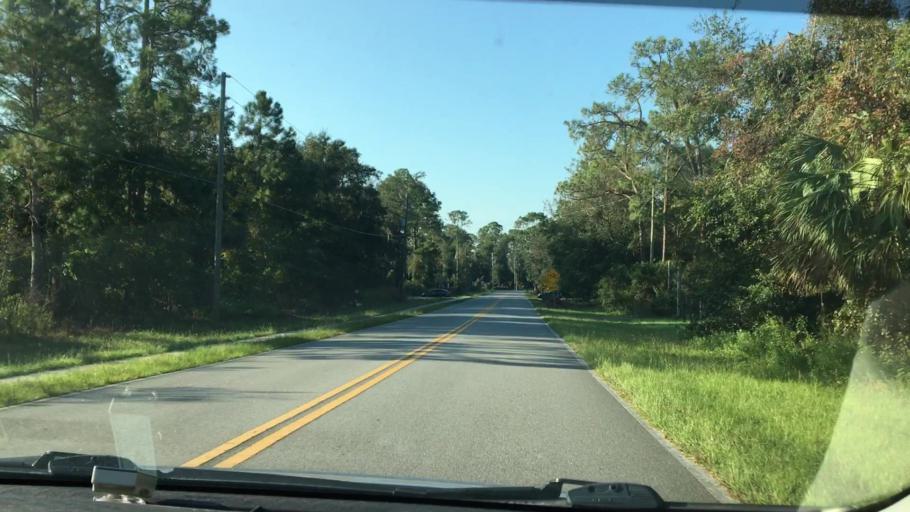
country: US
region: Florida
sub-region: Volusia County
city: Deltona
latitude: 28.8624
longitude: -81.2318
